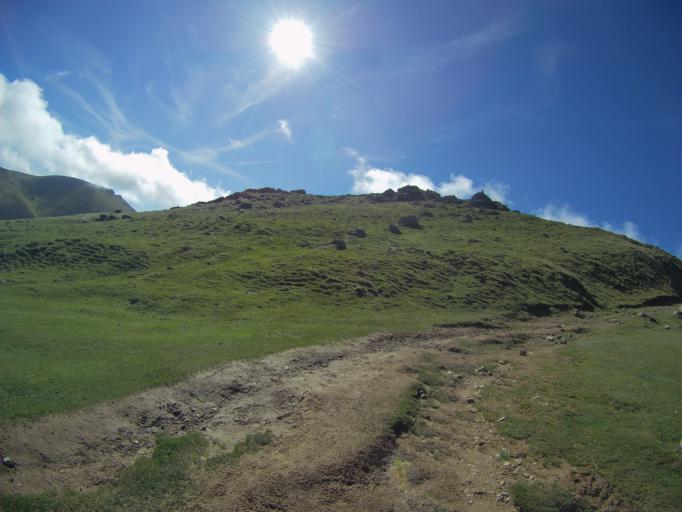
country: ES
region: Navarre
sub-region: Provincia de Navarra
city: Orbara
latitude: 43.0552
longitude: -1.2663
